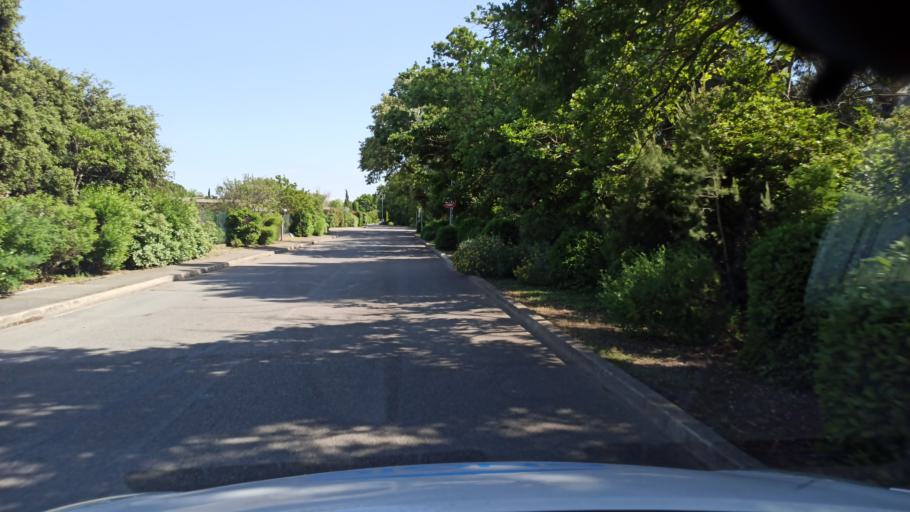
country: FR
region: Provence-Alpes-Cote d'Azur
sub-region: Departement du Vaucluse
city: Vedene
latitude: 43.9600
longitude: 4.8957
